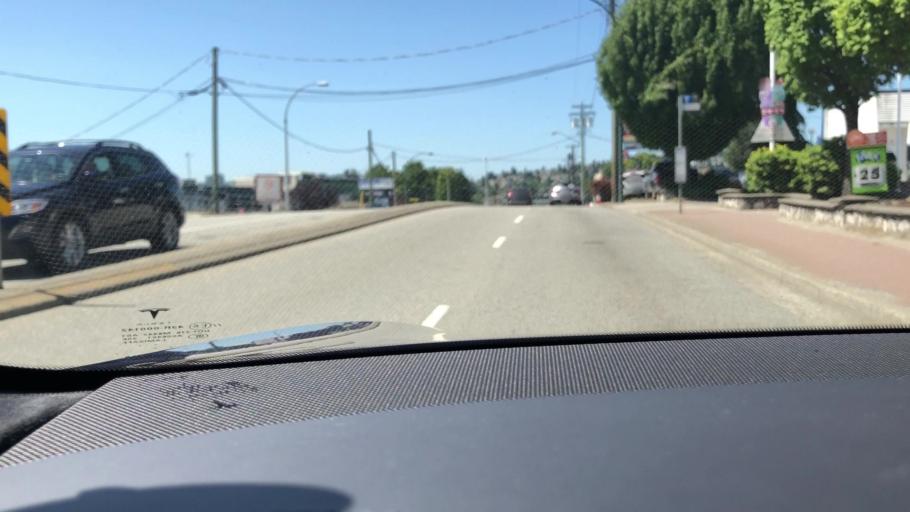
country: CA
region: British Columbia
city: New Westminster
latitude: 49.2361
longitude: -122.8733
